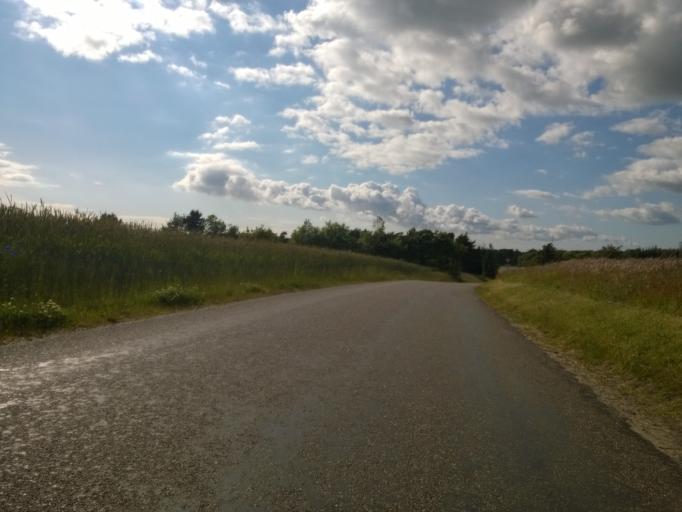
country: DK
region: Central Jutland
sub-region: Holstebro Kommune
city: Vinderup
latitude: 56.5128
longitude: 8.8110
